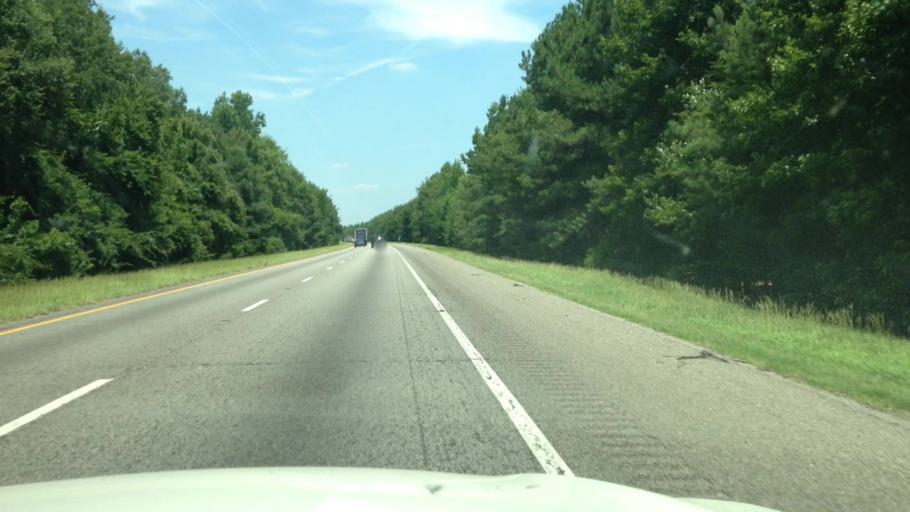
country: US
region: South Carolina
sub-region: Dillon County
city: Latta
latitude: 34.3187
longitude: -79.5905
